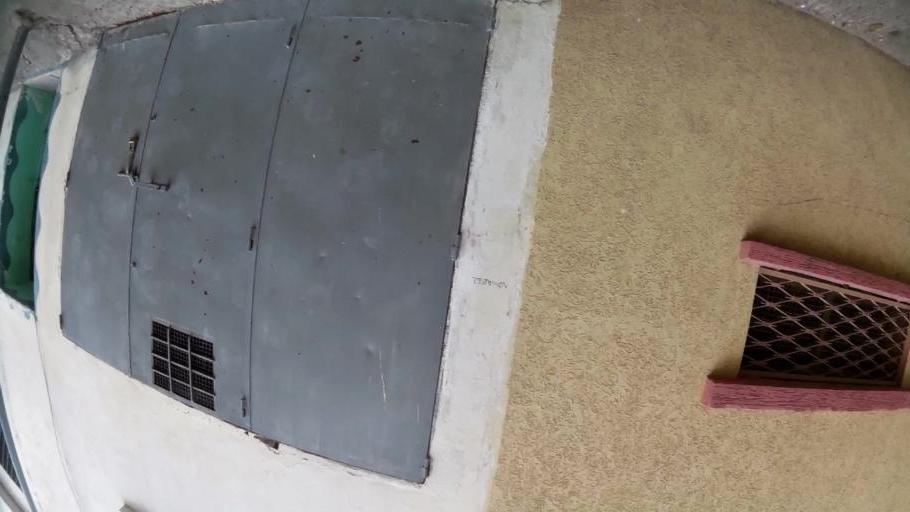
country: MA
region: Tanger-Tetouan
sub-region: Tanger-Assilah
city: Tangier
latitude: 35.7610
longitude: -5.8266
